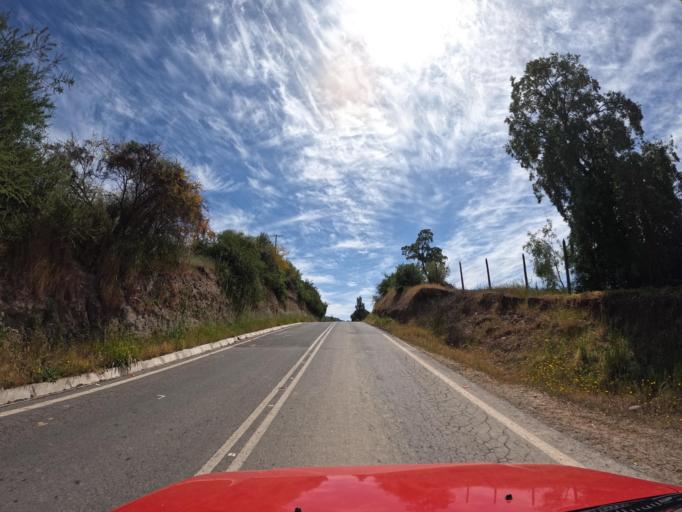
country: CL
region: Maule
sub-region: Provincia de Talca
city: Talca
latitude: -35.0136
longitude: -71.7802
